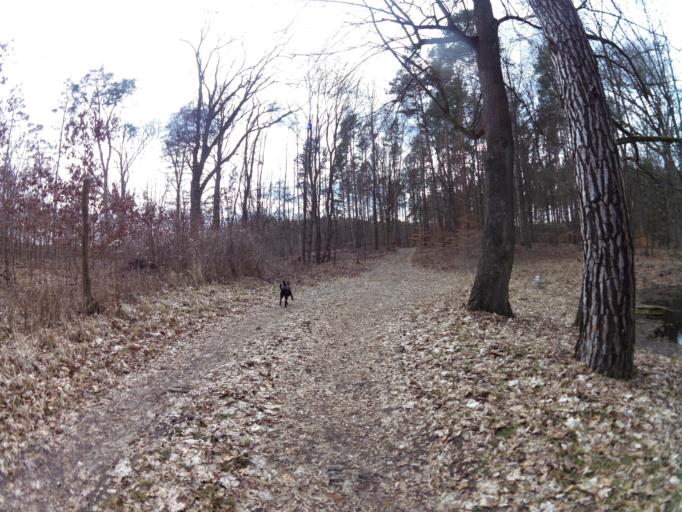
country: PL
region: Lubusz
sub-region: Powiat gorzowski
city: Lubiszyn
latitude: 52.7785
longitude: 14.8446
